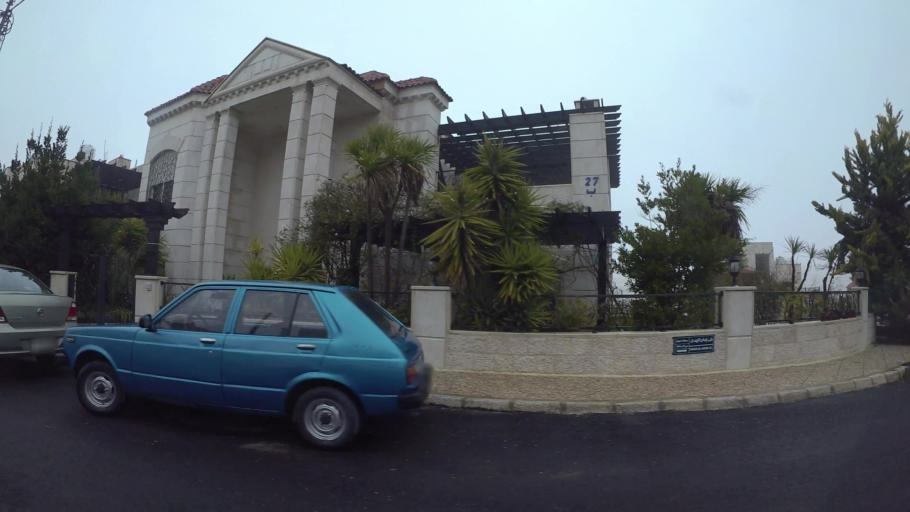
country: JO
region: Amman
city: Al Jubayhah
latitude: 32.0121
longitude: 35.8345
